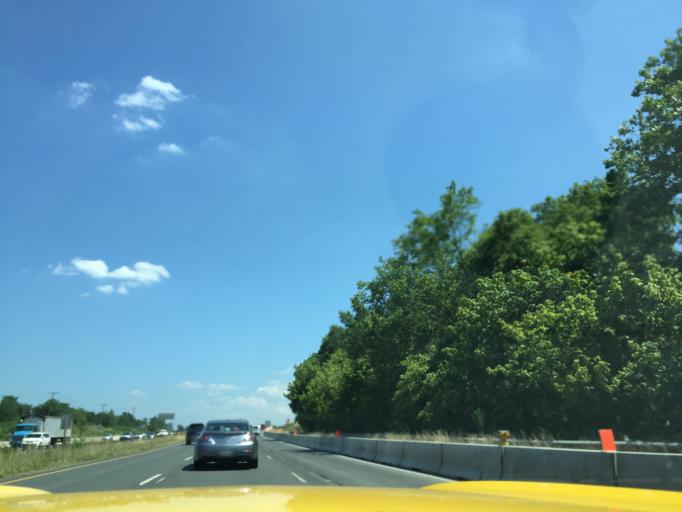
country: US
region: Virginia
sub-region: Loudoun County
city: Belmont
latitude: 39.0856
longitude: -77.5106
